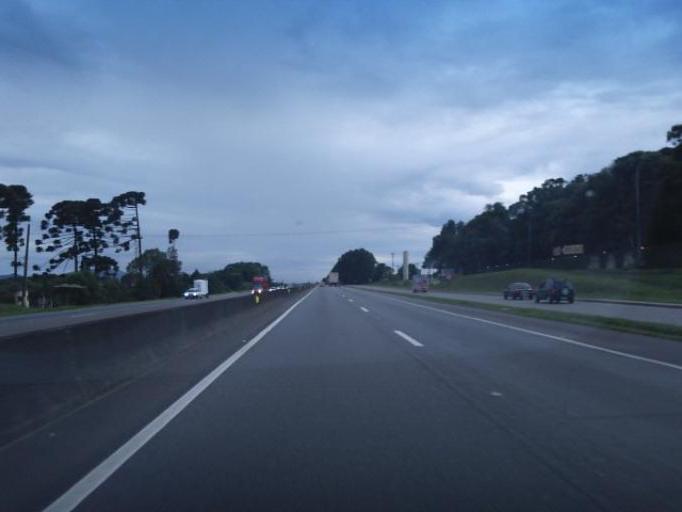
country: BR
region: Parana
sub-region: Sao Jose Dos Pinhais
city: Sao Jose dos Pinhais
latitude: -25.6531
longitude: -49.1571
